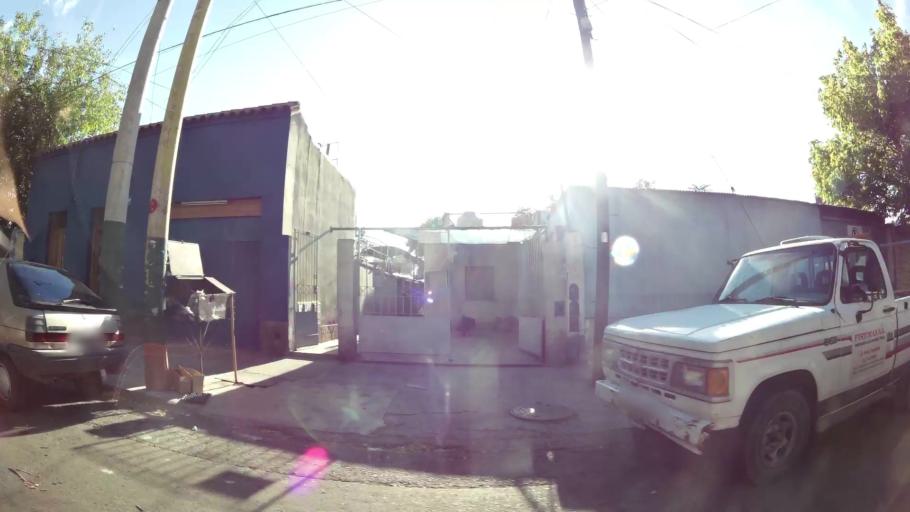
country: AR
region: Mendoza
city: Mendoza
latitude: -32.9067
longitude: -68.8288
